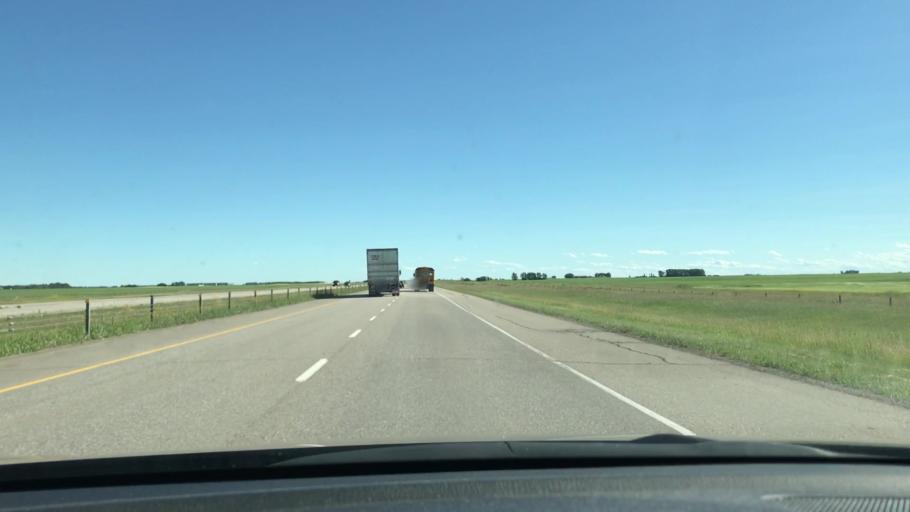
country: CA
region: Alberta
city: Olds
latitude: 51.7019
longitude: -114.0256
